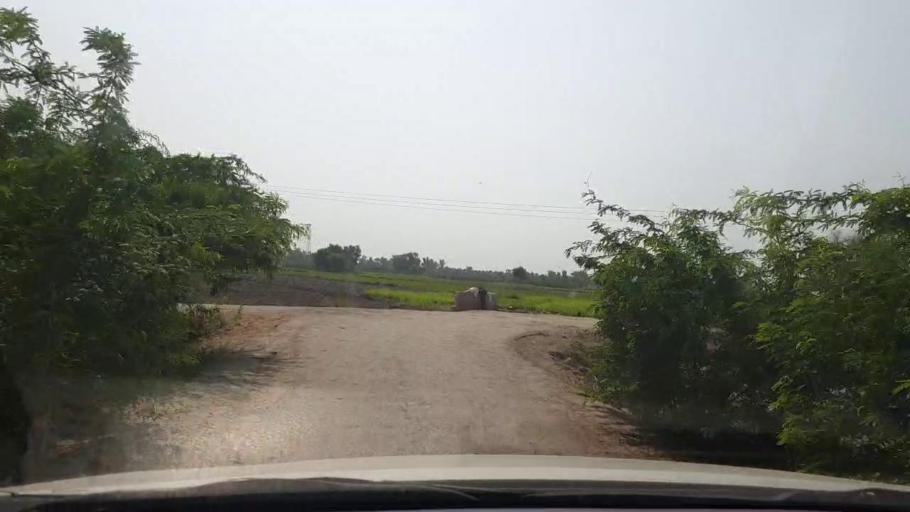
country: PK
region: Sindh
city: Shikarpur
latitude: 27.9792
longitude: 68.6744
